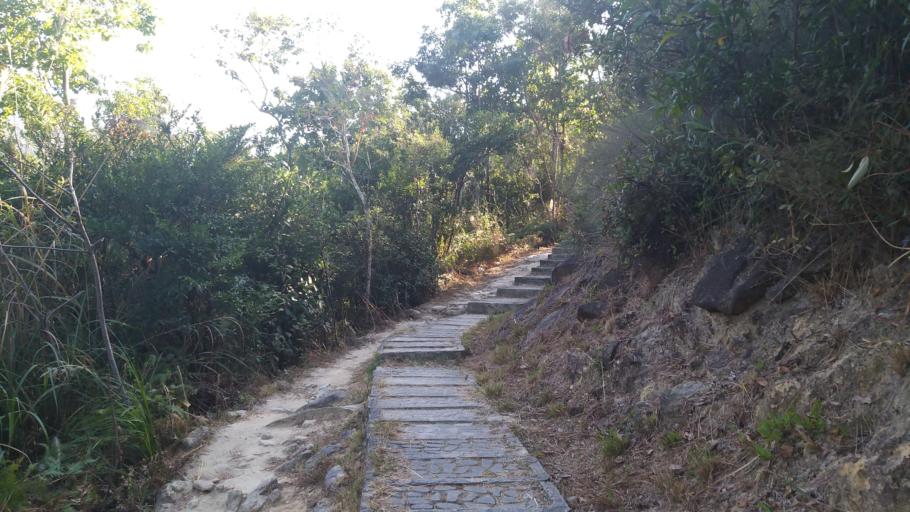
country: HK
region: Tuen Mun
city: Tuen Mun
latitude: 22.4064
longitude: 113.9886
